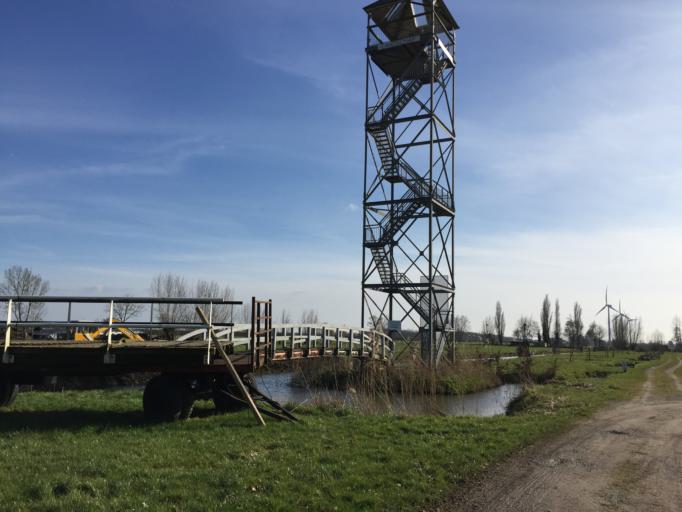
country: NL
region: Utrecht
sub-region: Gemeente Lopik
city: Lopik
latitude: 52.0027
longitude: 4.9526
